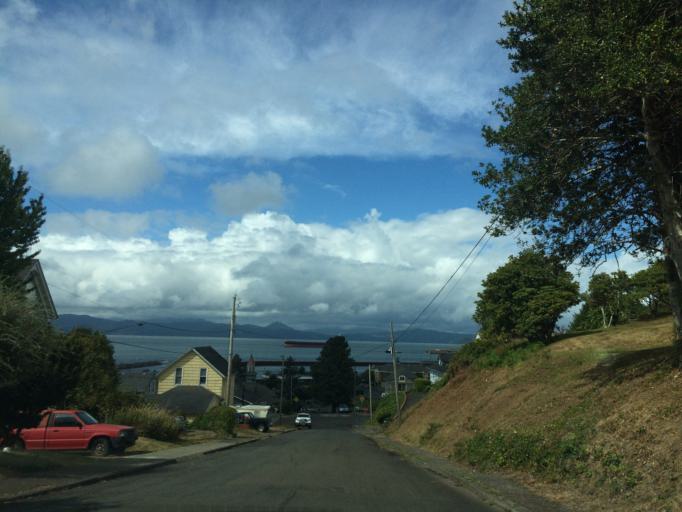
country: US
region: Oregon
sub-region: Clatsop County
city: Astoria
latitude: 46.1904
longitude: -123.8059
